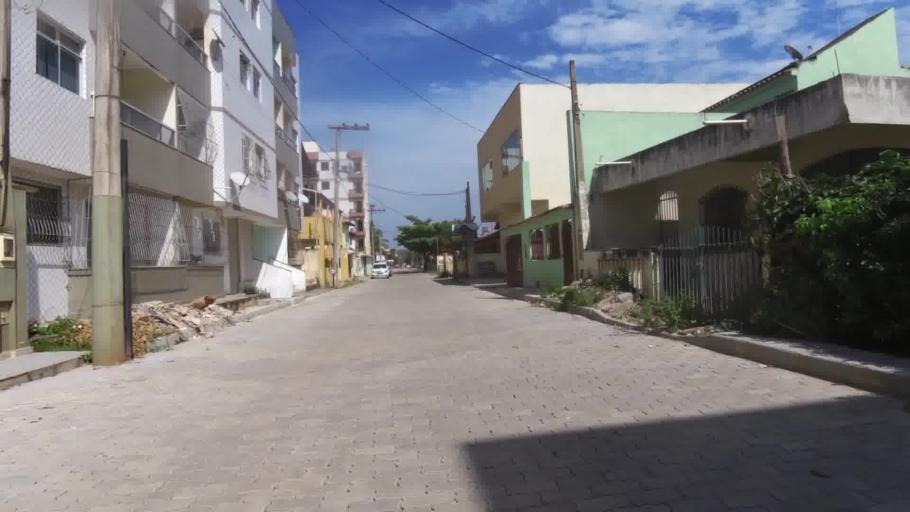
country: BR
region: Espirito Santo
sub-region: Piuma
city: Piuma
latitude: -20.8443
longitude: -40.7443
